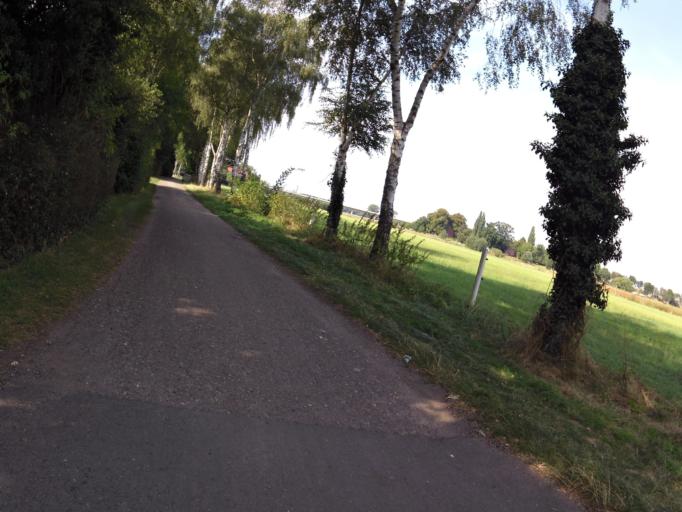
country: DE
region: North Rhine-Westphalia
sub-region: Regierungsbezirk Detmold
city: Petershagen
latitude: 52.3751
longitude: 8.9748
